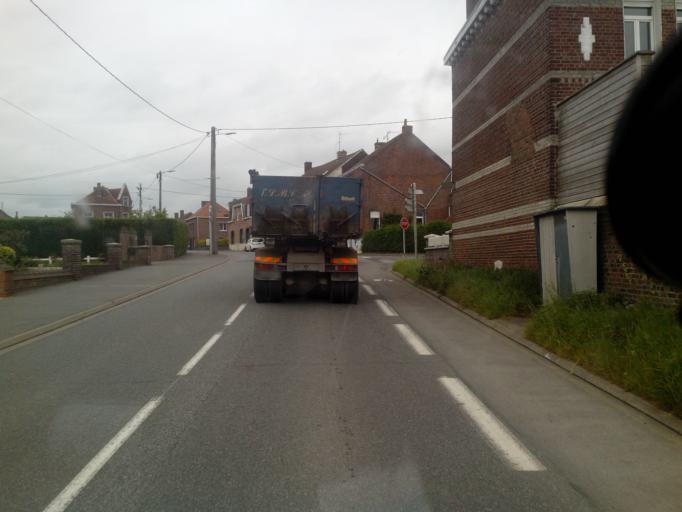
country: FR
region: Nord-Pas-de-Calais
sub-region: Departement du Nord
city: Vieux-Berquin
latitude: 50.7262
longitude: 2.6327
